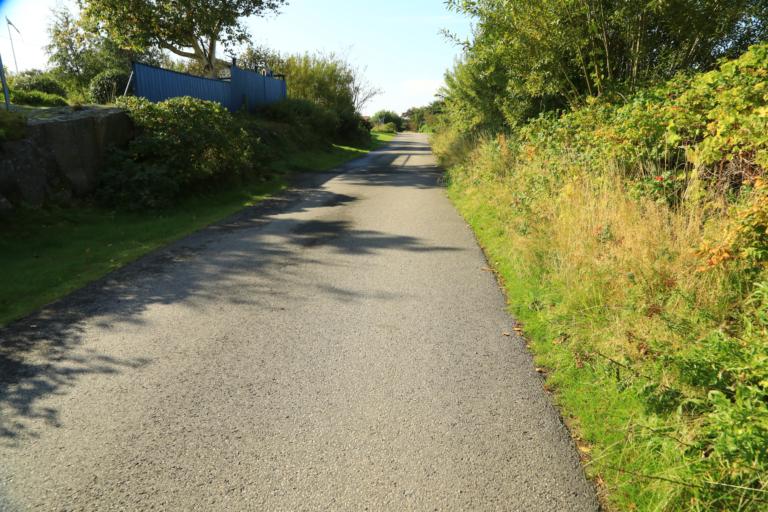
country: SE
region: Halland
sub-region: Varbergs Kommun
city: Varberg
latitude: 57.1152
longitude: 12.2212
